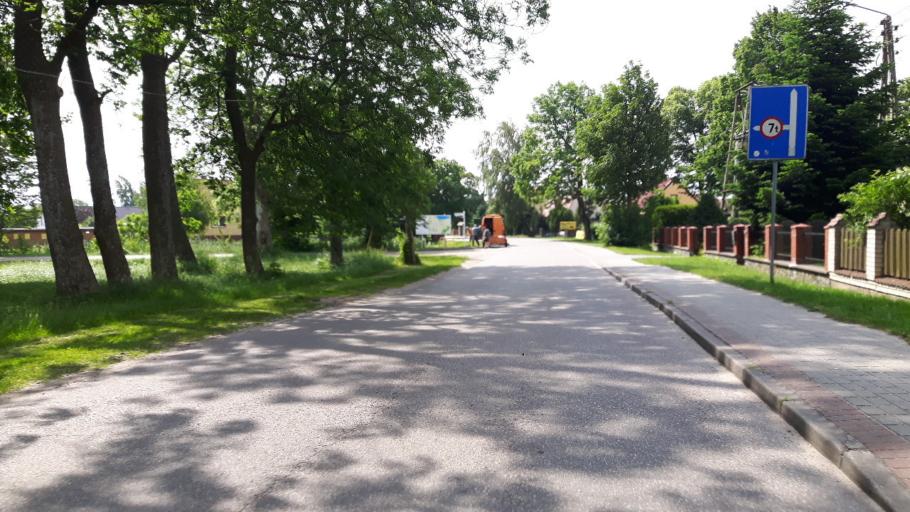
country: PL
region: Pomeranian Voivodeship
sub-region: Powiat leborski
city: Leba
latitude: 54.7512
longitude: 17.5878
